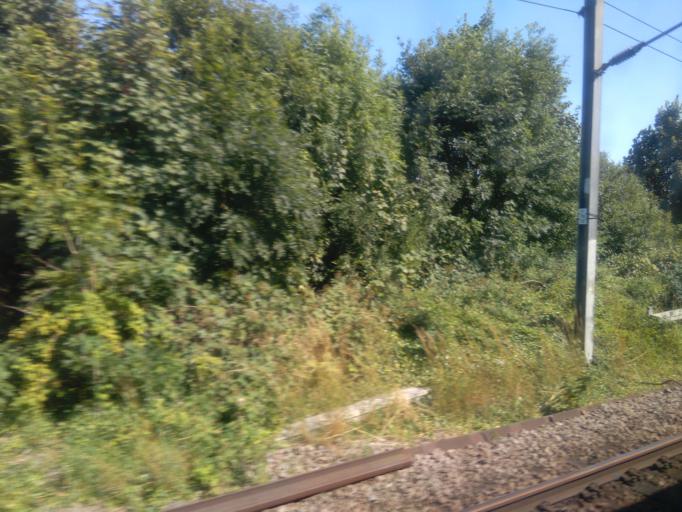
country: GB
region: England
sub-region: Bedford
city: Bedford
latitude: 52.1294
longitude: -0.4770
